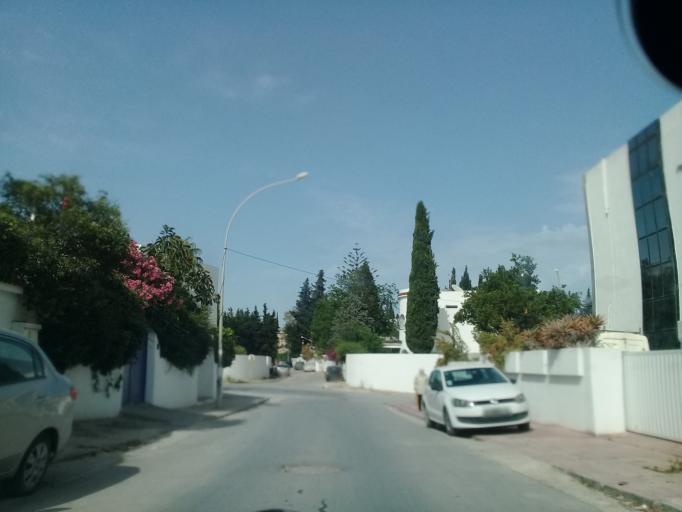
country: TN
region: Tunis
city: Tunis
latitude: 36.8501
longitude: 10.1596
